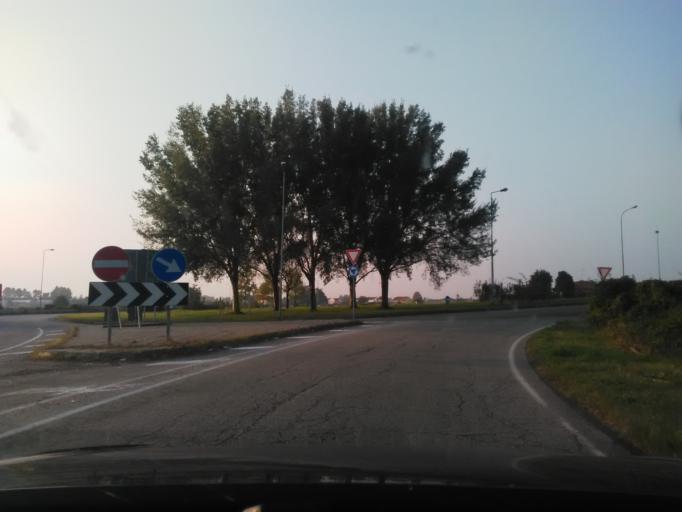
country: IT
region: Piedmont
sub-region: Provincia di Alessandria
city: Casale Monferrato
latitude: 45.1520
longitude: 8.4408
